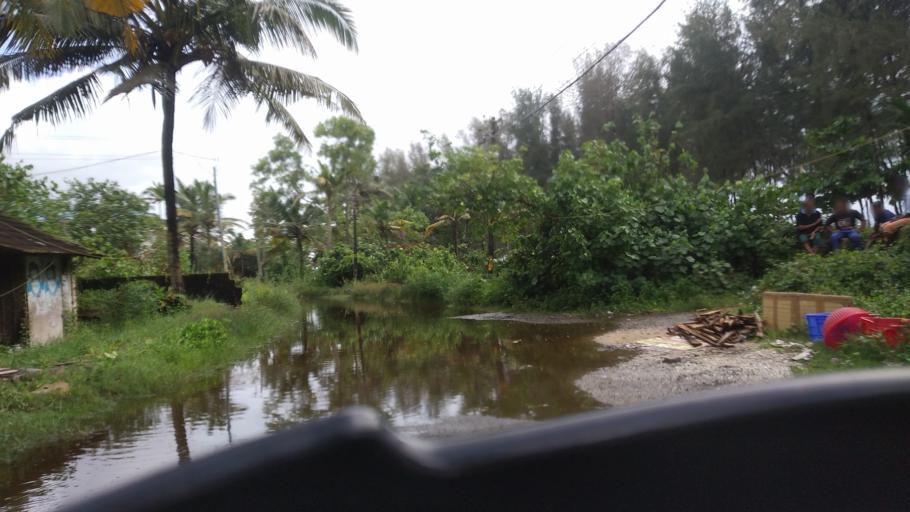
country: IN
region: Kerala
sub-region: Ernakulam
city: Elur
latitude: 10.1039
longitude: 76.1890
